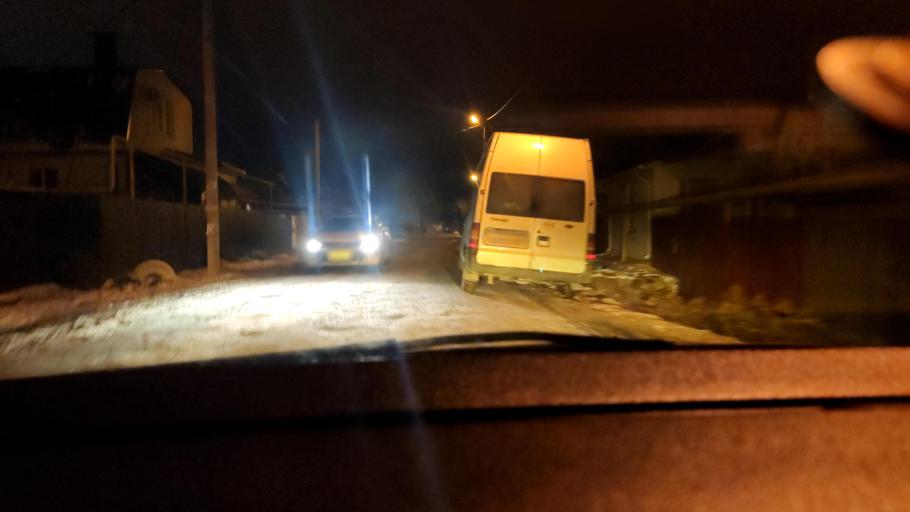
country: RU
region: Voronezj
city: Pridonskoy
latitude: 51.6690
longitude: 39.0809
